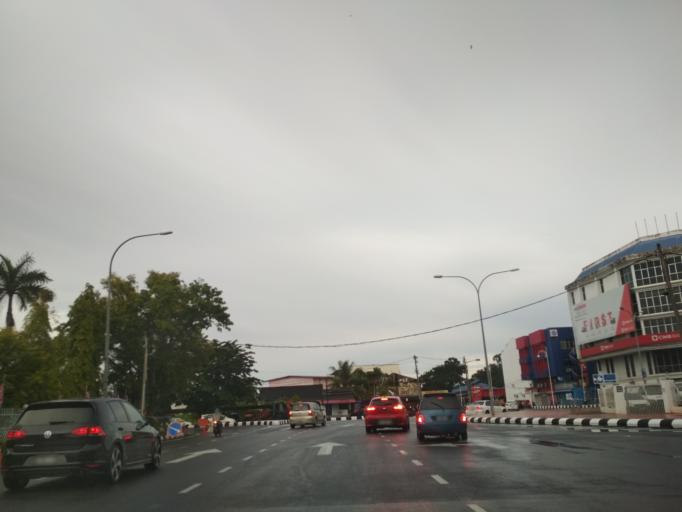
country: MY
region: Perlis
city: Kangar
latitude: 6.4400
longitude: 100.1943
